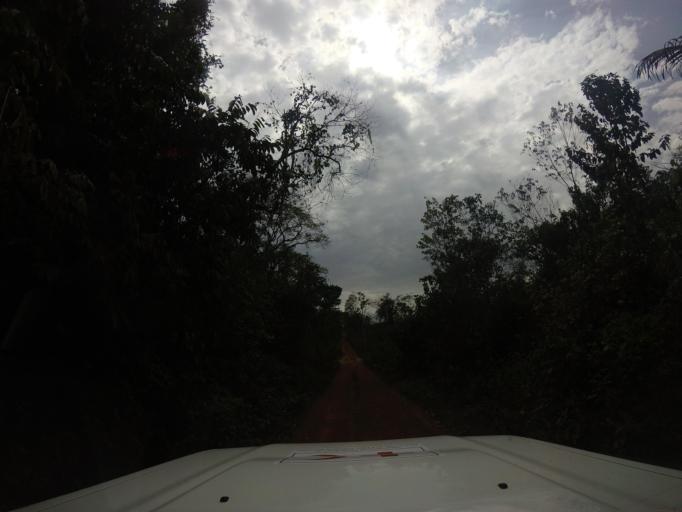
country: SL
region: Southern Province
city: Zimmi
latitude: 7.2163
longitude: -11.1858
